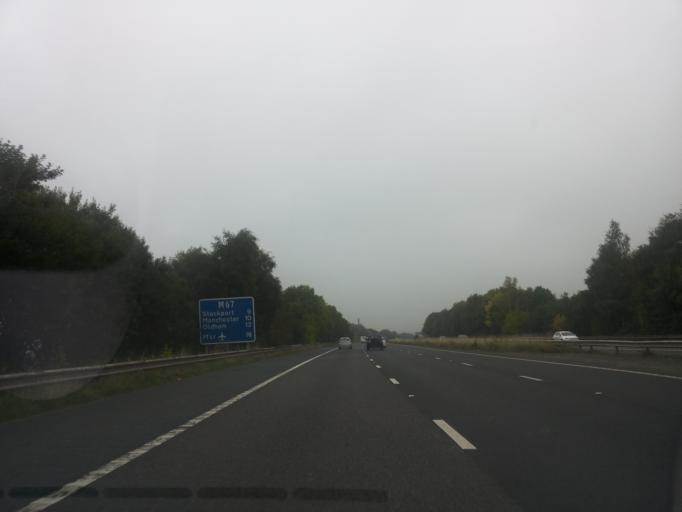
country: GB
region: England
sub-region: Borough of Tameside
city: Stalybridge
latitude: 53.4549
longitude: -2.0357
